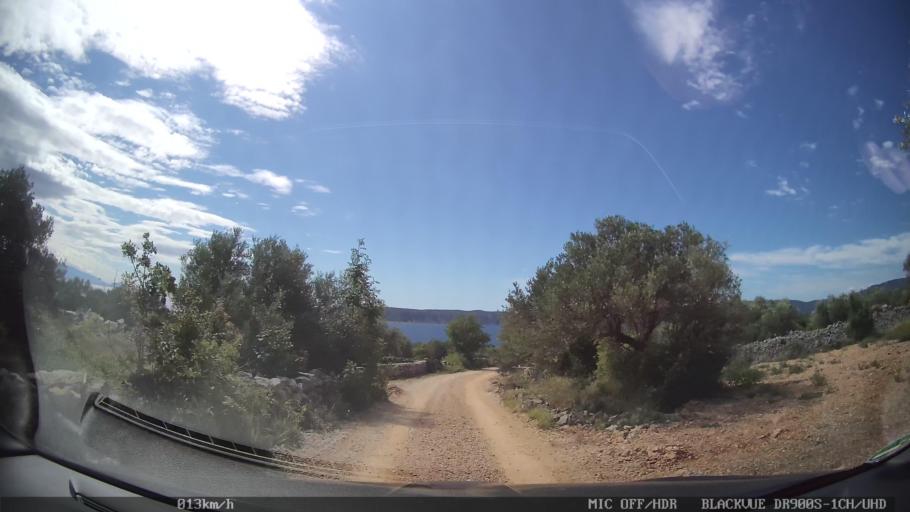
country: HR
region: Primorsko-Goranska
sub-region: Grad Krk
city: Krk
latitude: 45.0279
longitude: 14.5251
